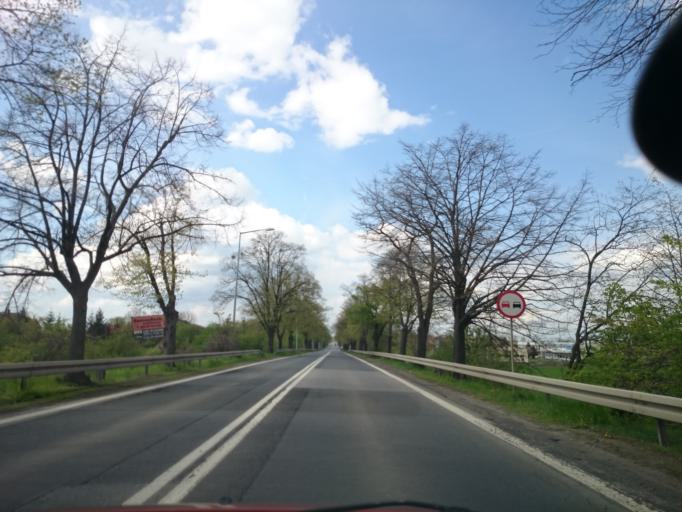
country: PL
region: Opole Voivodeship
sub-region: Powiat opolski
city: Opole
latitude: 50.6519
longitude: 17.9654
